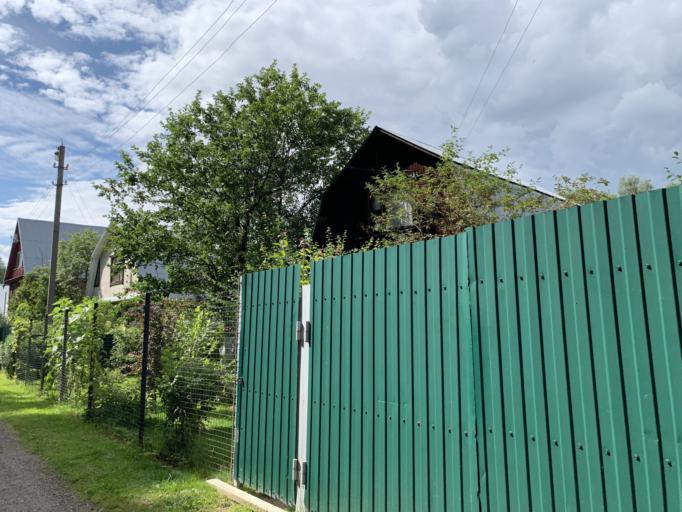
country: RU
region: Moskovskaya
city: Podosinki
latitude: 56.1802
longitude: 37.5750
